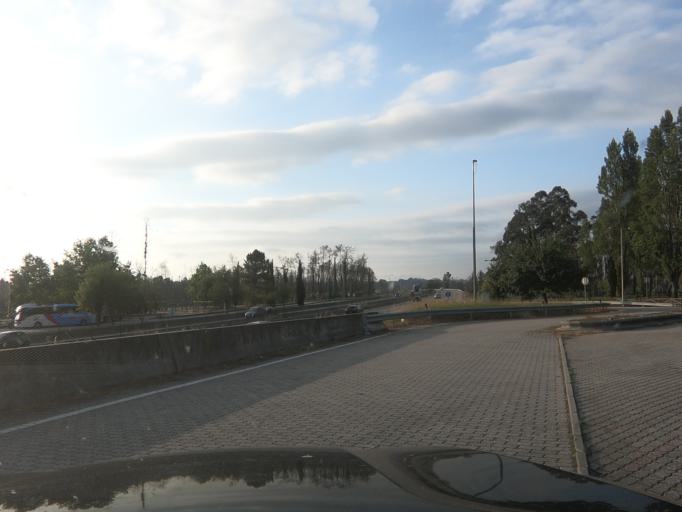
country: PT
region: Aveiro
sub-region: Oliveira do Bairro
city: Oia
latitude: 40.5505
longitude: -8.5597
